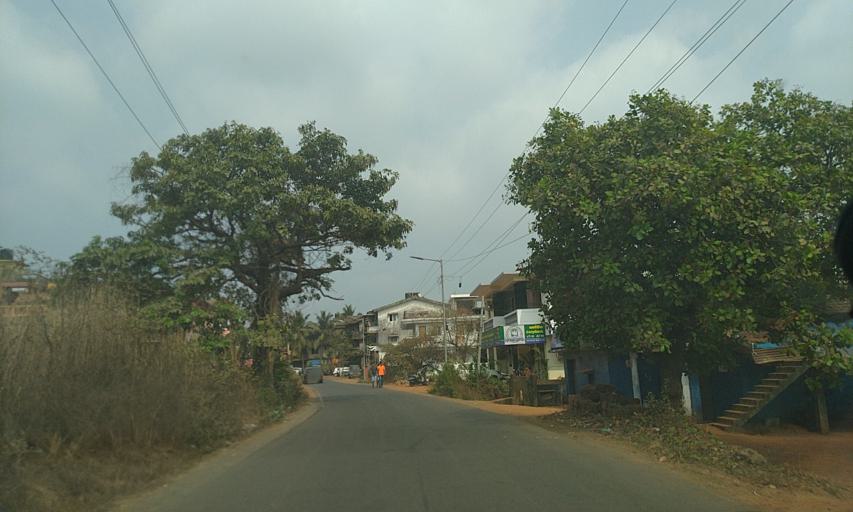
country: IN
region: Goa
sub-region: South Goa
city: Raia
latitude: 15.3067
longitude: 73.9496
